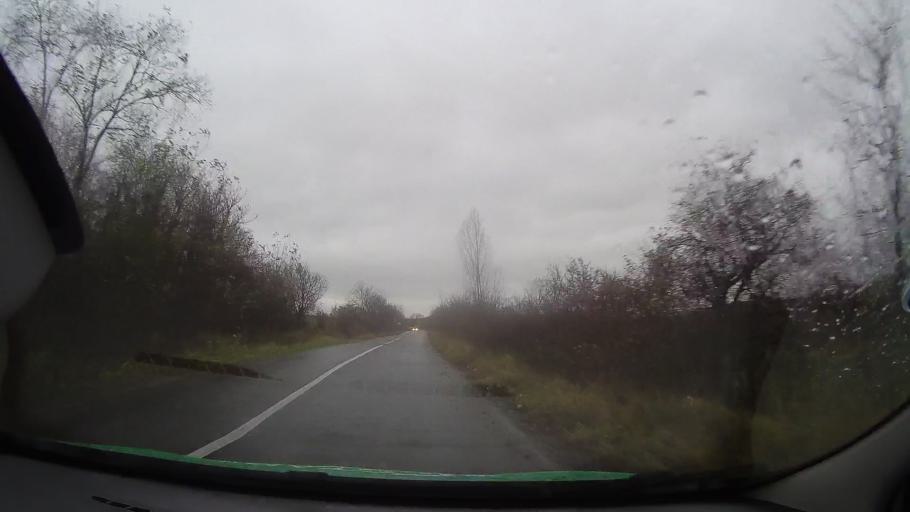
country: RO
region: Mures
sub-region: Comuna Brancovenesti
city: Valenii de Mures
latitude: 46.8990
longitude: 24.7935
